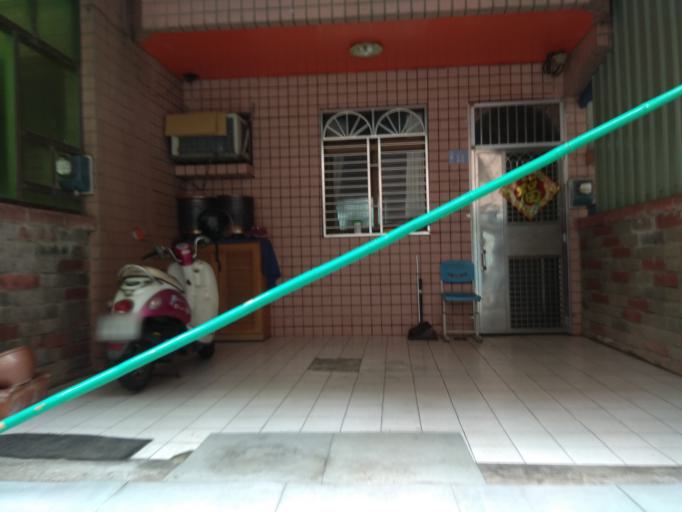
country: TW
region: Taiwan
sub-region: Hsinchu
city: Zhubei
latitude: 24.9838
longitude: 121.0522
